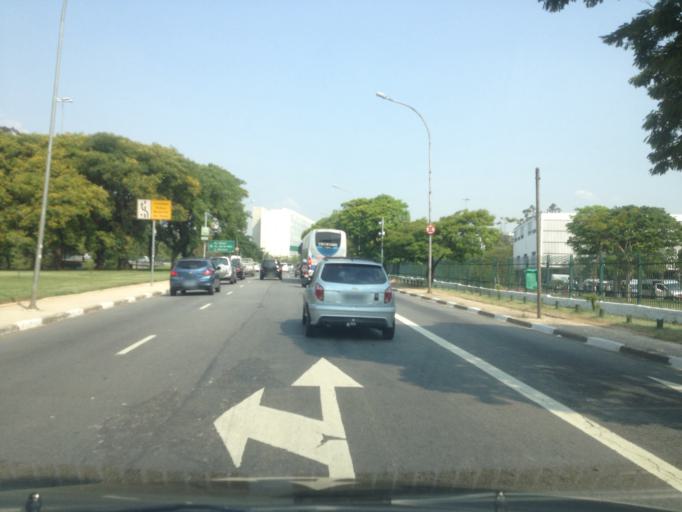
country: BR
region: Sao Paulo
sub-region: Sao Paulo
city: Sao Paulo
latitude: -23.5863
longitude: -46.6545
